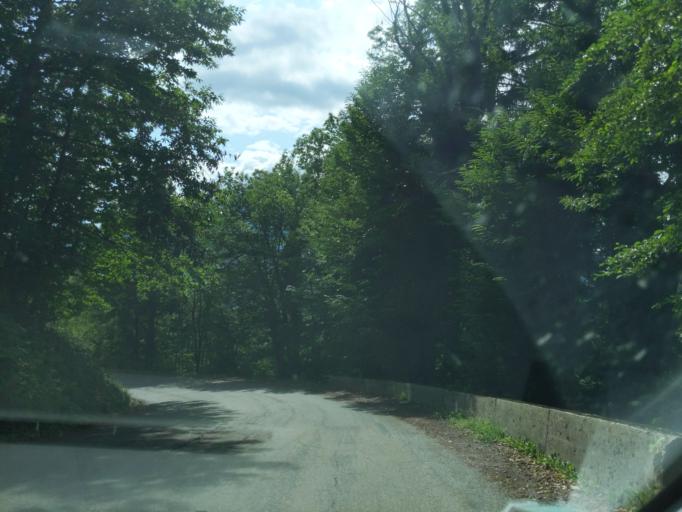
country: FR
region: Rhone-Alpes
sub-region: Departement de la Savoie
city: Ugine
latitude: 45.7401
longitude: 6.4359
